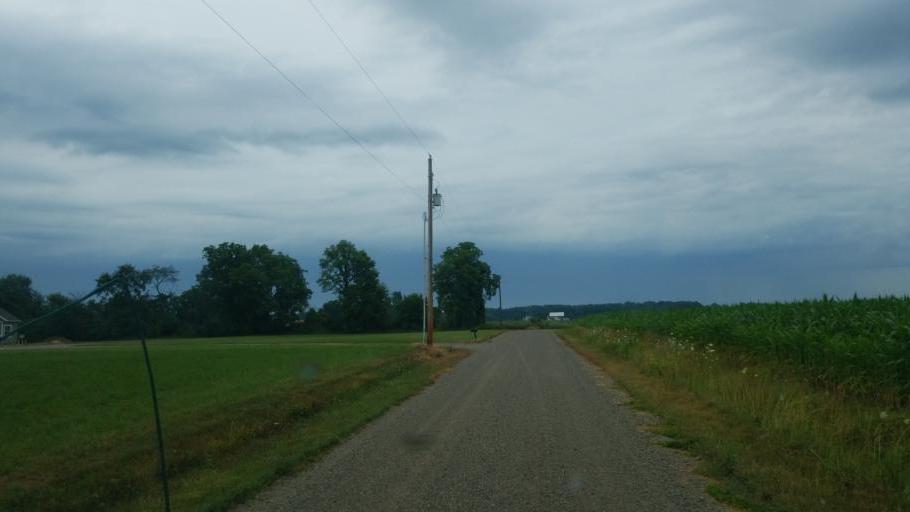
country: US
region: Indiana
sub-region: Steuben County
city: Hamilton
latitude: 41.5058
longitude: -84.9128
